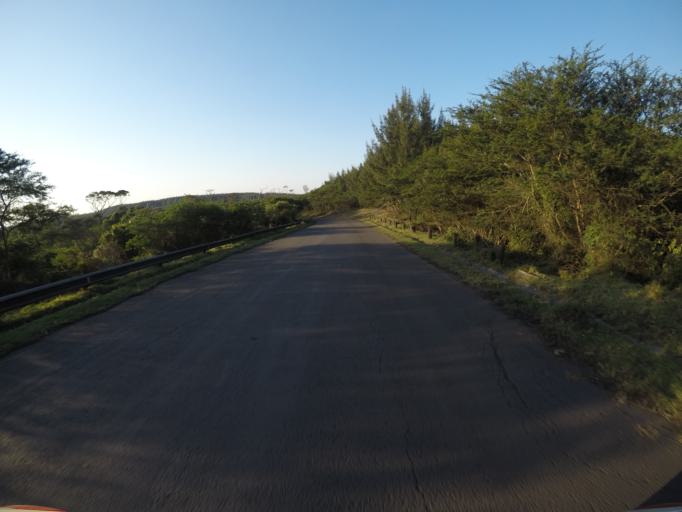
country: ZA
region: KwaZulu-Natal
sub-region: uThungulu District Municipality
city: KwaMbonambi
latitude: -28.6955
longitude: 32.2100
